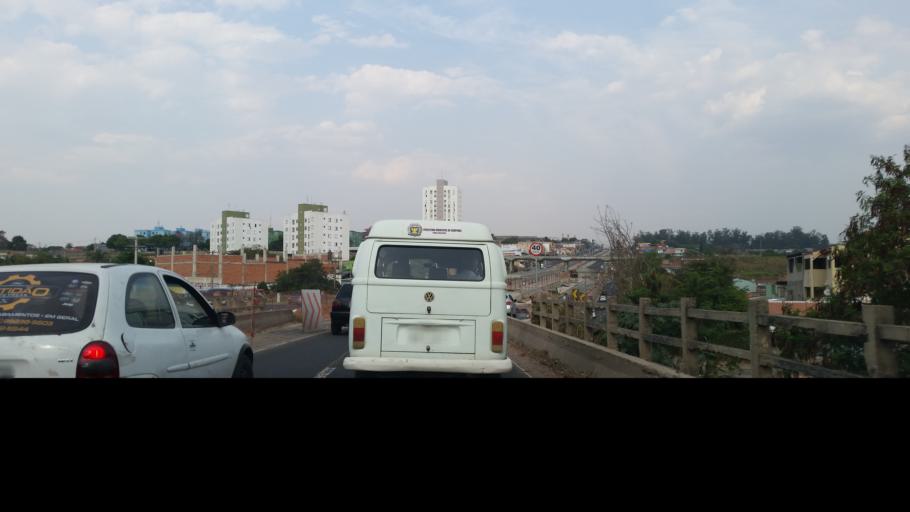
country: BR
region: Sao Paulo
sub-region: Hortolandia
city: Hortolandia
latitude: -22.9370
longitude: -47.1620
